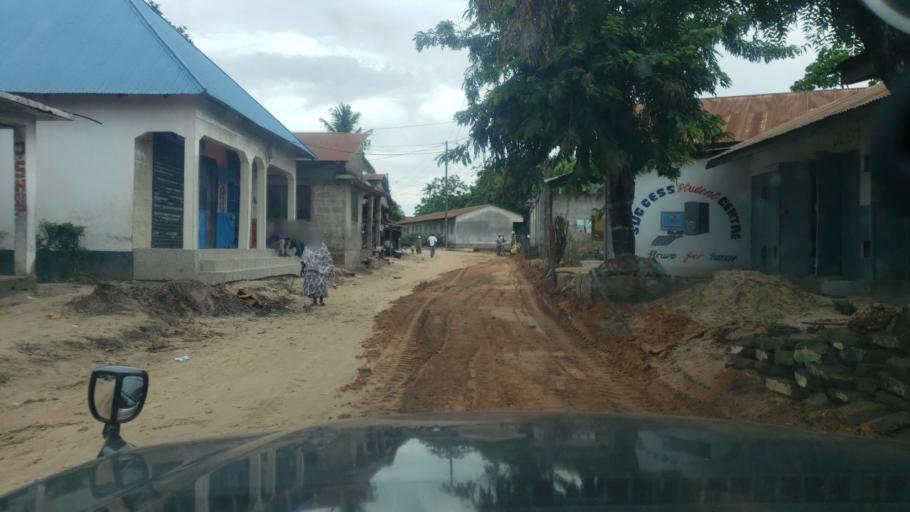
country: TZ
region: Pwani
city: Vikindu
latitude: -6.9247
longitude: 39.2519
